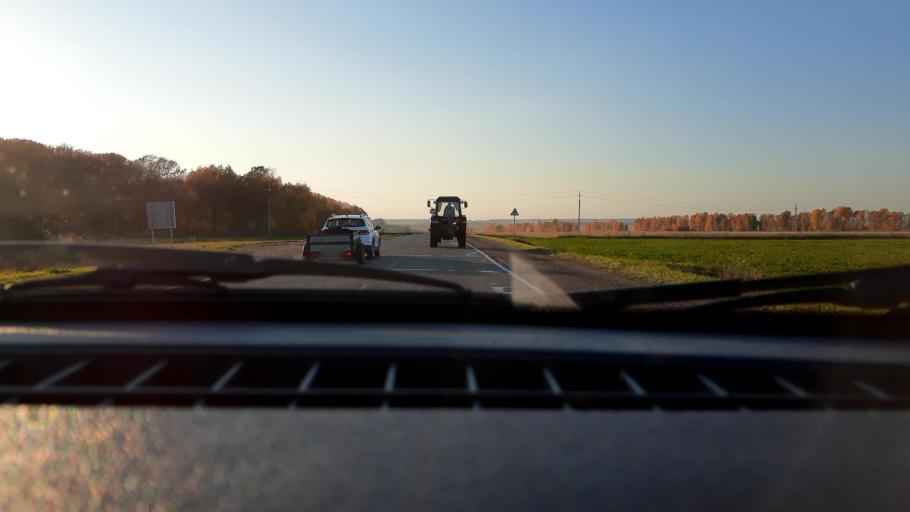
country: RU
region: Bashkortostan
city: Asanovo
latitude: 54.8256
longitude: 55.6442
